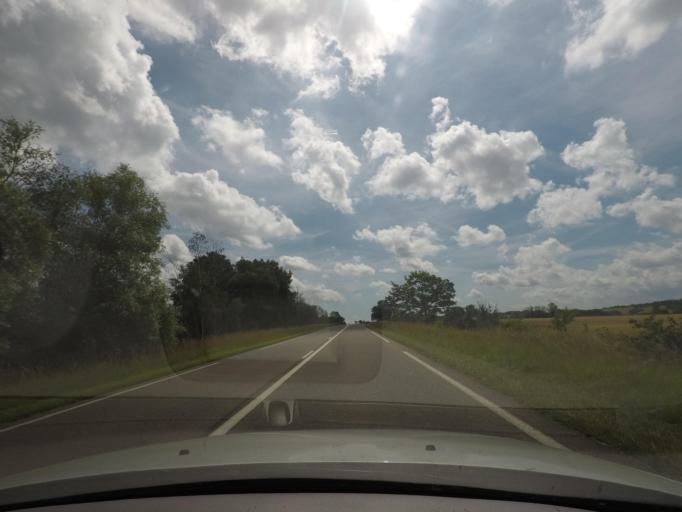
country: FR
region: Alsace
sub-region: Departement du Bas-Rhin
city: Drulingen
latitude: 48.8846
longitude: 7.1452
